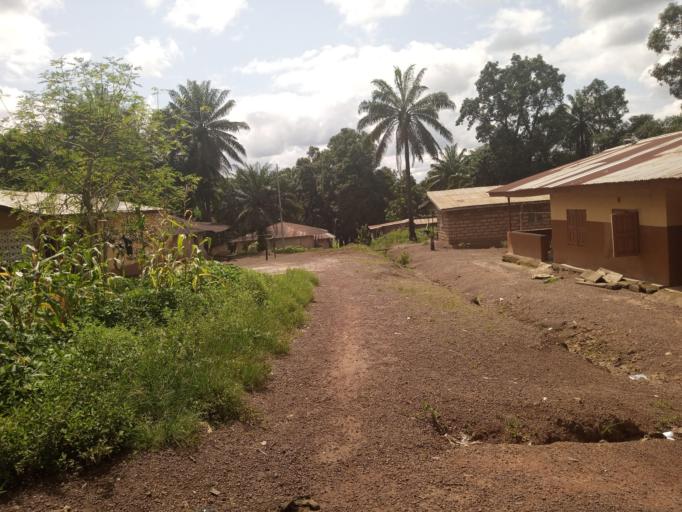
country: SL
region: Northern Province
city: Kamakwie
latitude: 9.4946
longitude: -12.2460
